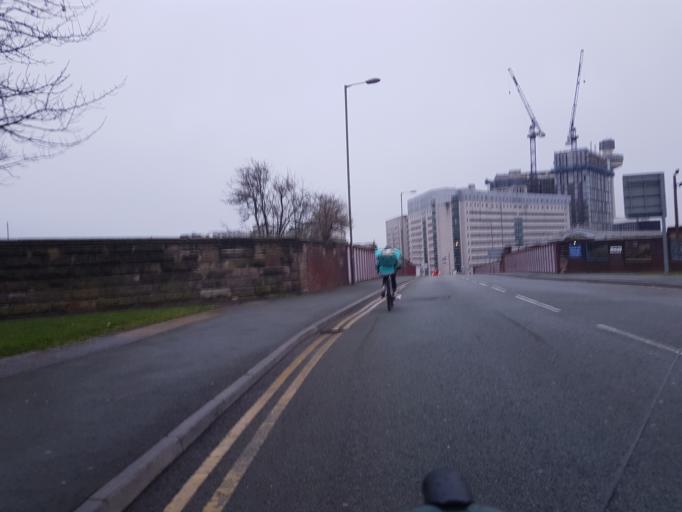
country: GB
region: England
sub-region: Liverpool
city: Liverpool
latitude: 53.4077
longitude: -2.9740
